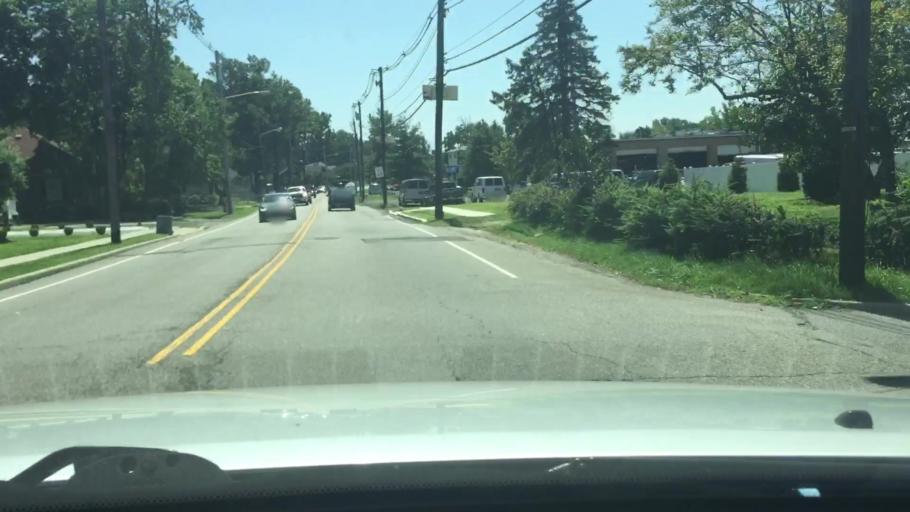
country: US
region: New Jersey
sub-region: Middlesex County
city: South River
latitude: 40.4520
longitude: -74.3944
